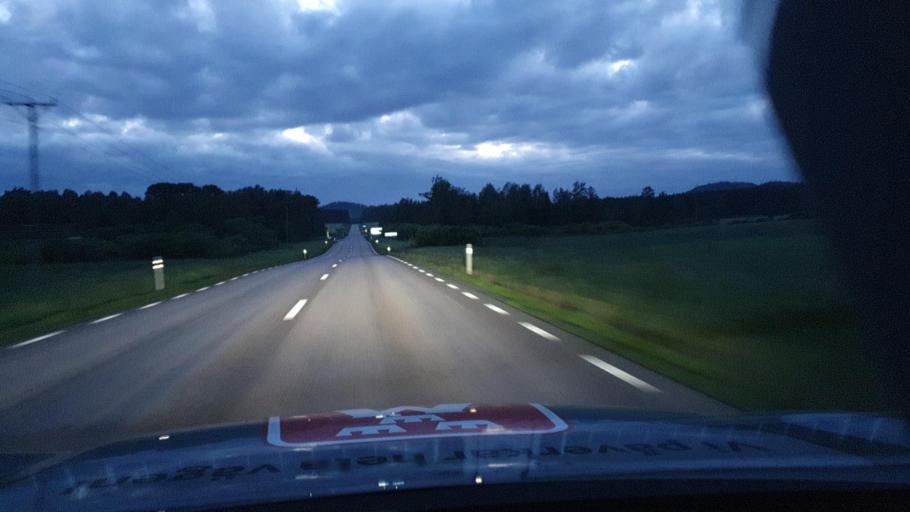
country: SE
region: OErebro
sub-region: Karlskoga Kommun
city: Karlskoga
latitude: 59.4371
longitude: 14.4085
